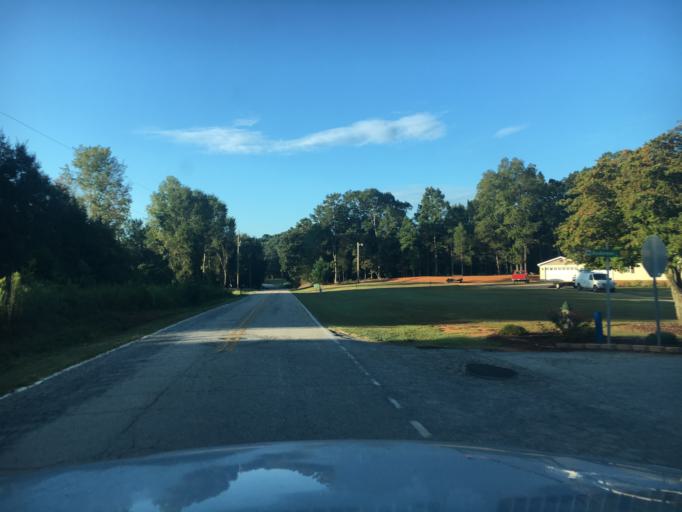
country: US
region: South Carolina
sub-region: Spartanburg County
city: Woodruff
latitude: 34.7557
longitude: -81.9612
